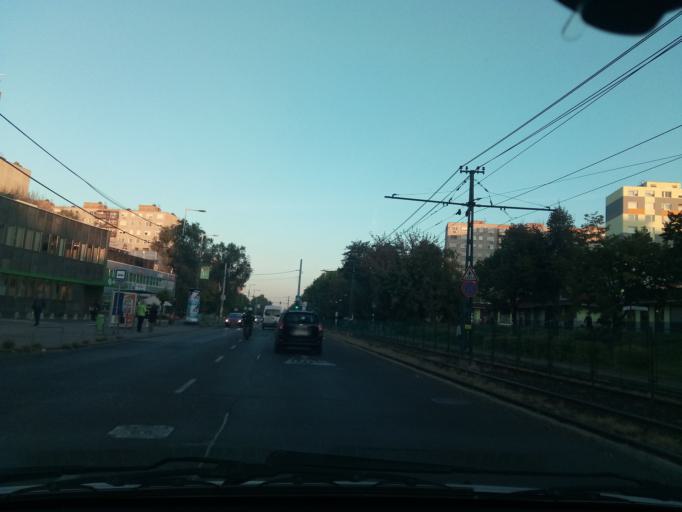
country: HU
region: Budapest
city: Budapest XIX. keruelet
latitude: 47.4543
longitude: 19.1519
